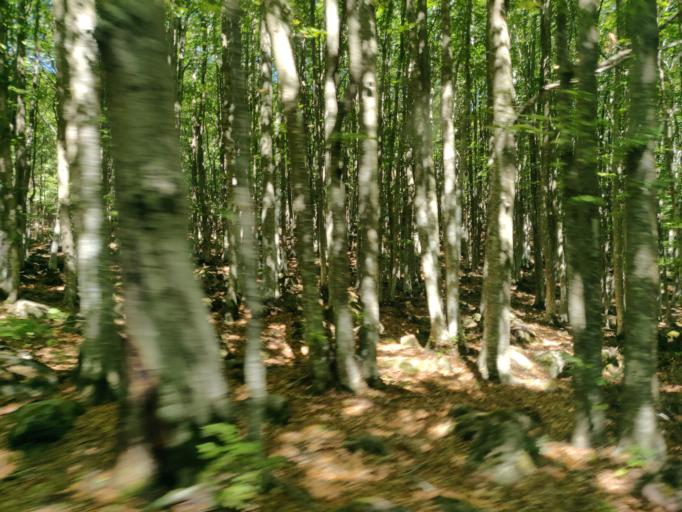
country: IT
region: Tuscany
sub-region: Provincia di Siena
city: Abbadia San Salvatore
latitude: 42.8835
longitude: 11.6232
